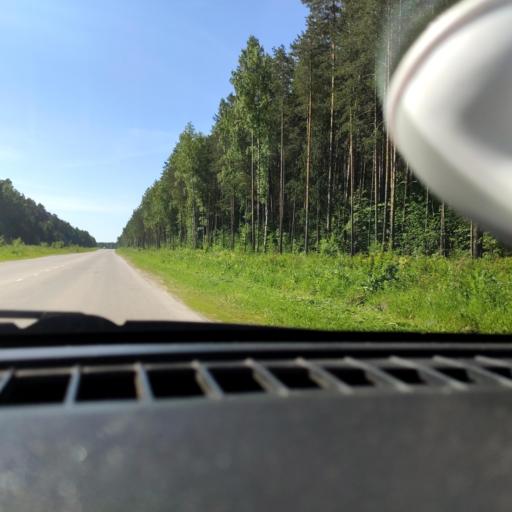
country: RU
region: Perm
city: Overyata
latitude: 58.0069
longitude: 55.8761
